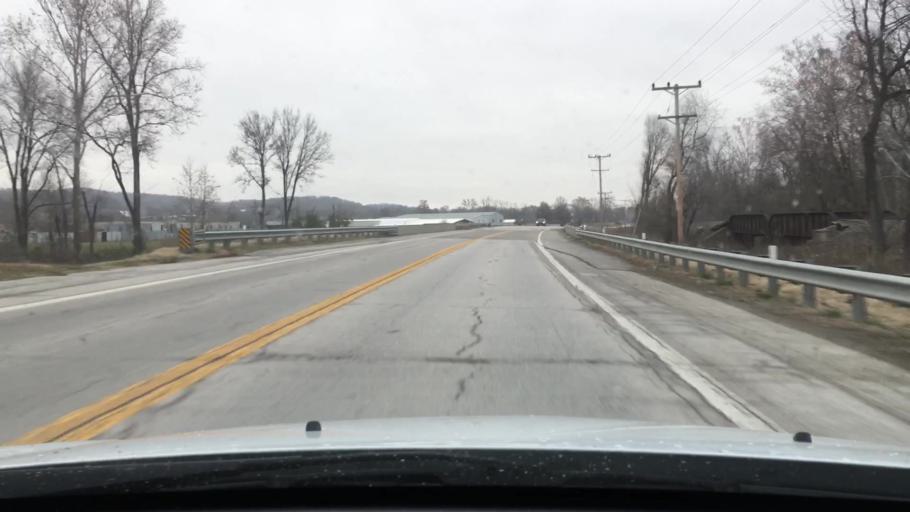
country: US
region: Missouri
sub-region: Pike County
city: Louisiana
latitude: 39.4119
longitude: -91.1012
